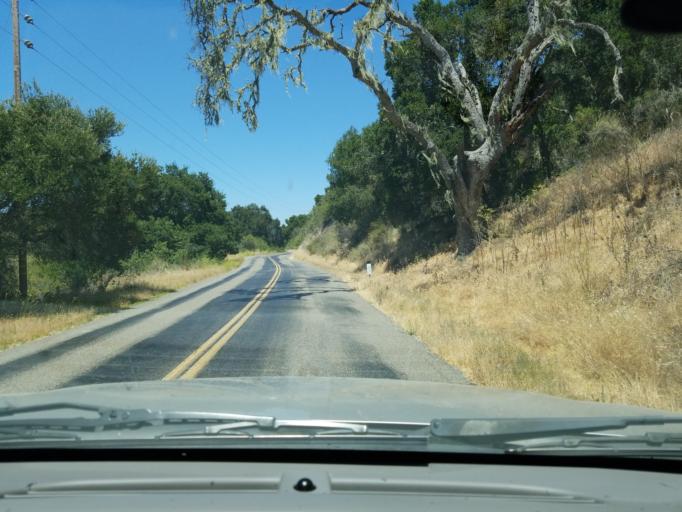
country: US
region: California
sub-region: Monterey County
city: Carmel Valley Village
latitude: 36.4235
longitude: -121.6169
